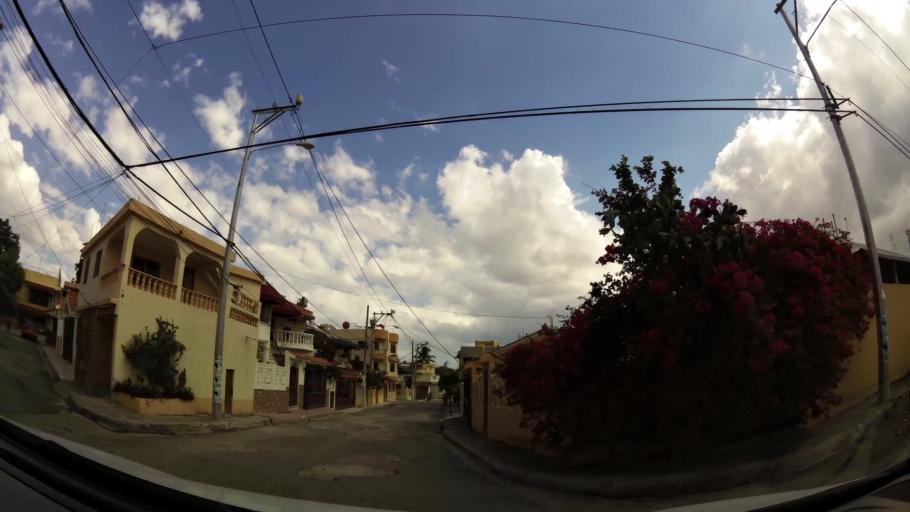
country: DO
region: Nacional
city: Ensanche Luperon
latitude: 18.5421
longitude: -69.9028
